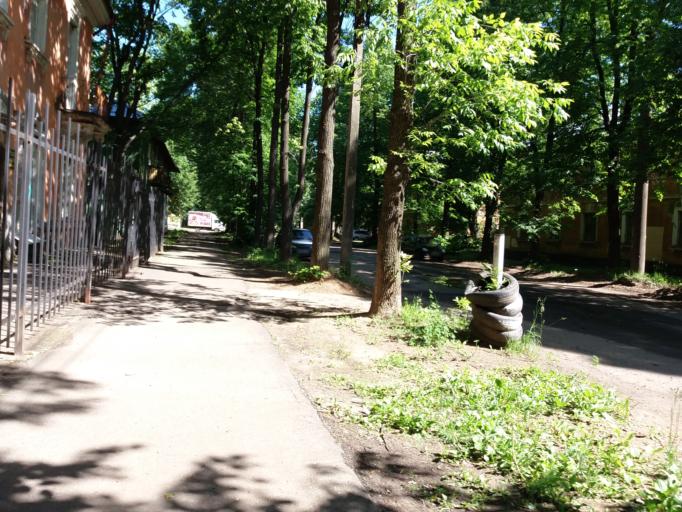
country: RU
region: Jaroslavl
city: Yaroslavl
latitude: 57.6399
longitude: 39.8347
